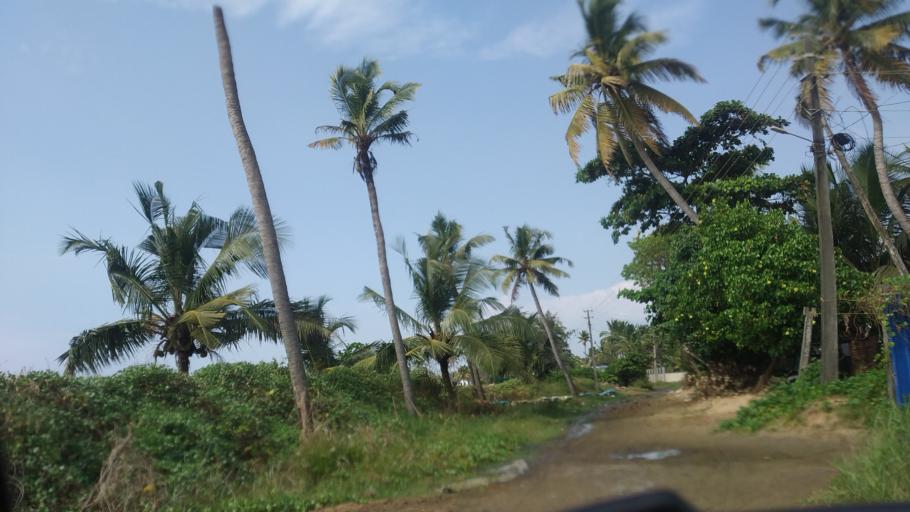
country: IN
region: Kerala
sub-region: Ernakulam
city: Elur
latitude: 10.0822
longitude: 76.1946
